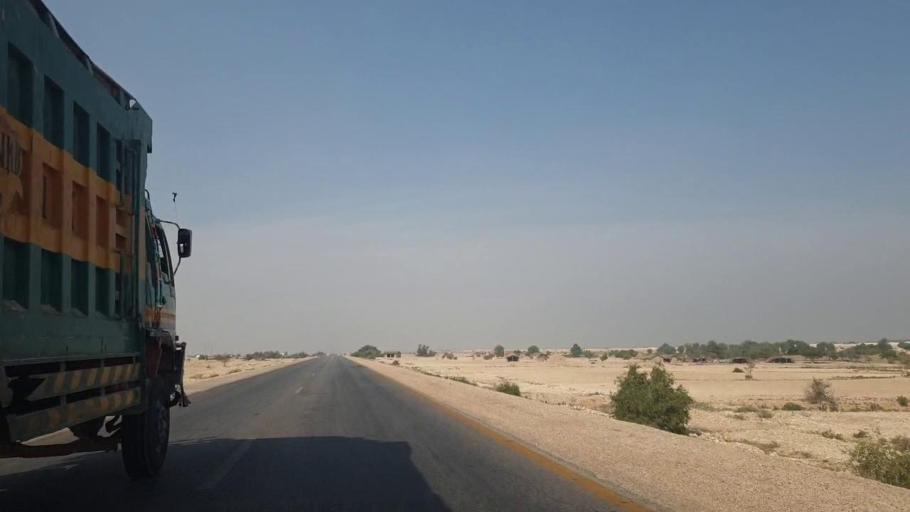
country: PK
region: Sindh
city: Hala
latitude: 25.8362
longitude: 68.2677
